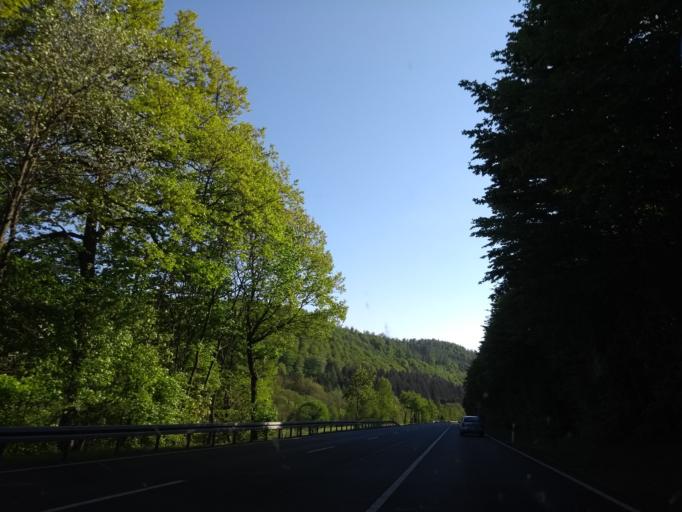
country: DE
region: Hesse
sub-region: Regierungsbezirk Giessen
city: Biedenkopf
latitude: 50.9359
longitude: 8.5358
